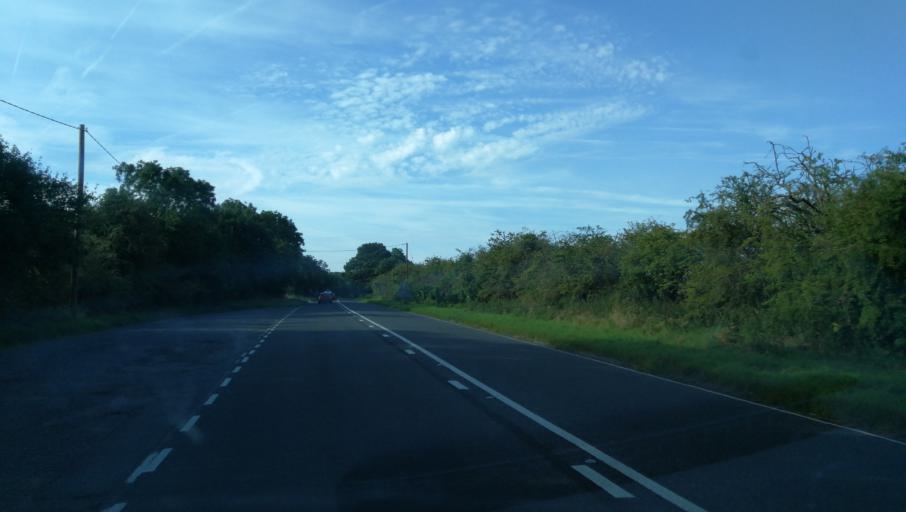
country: GB
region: England
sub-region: Oxfordshire
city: Deddington
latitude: 51.9536
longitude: -1.3183
